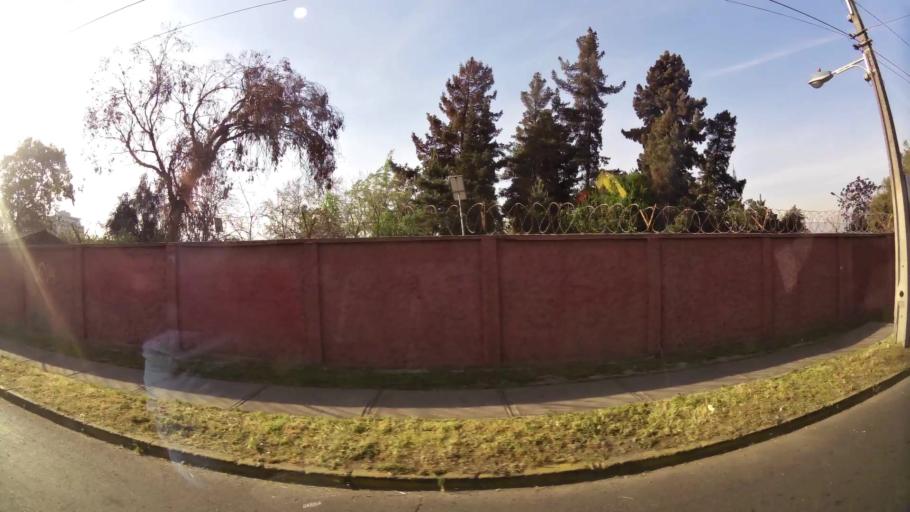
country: CL
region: Santiago Metropolitan
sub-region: Provincia de Santiago
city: La Pintana
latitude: -33.5229
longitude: -70.6068
